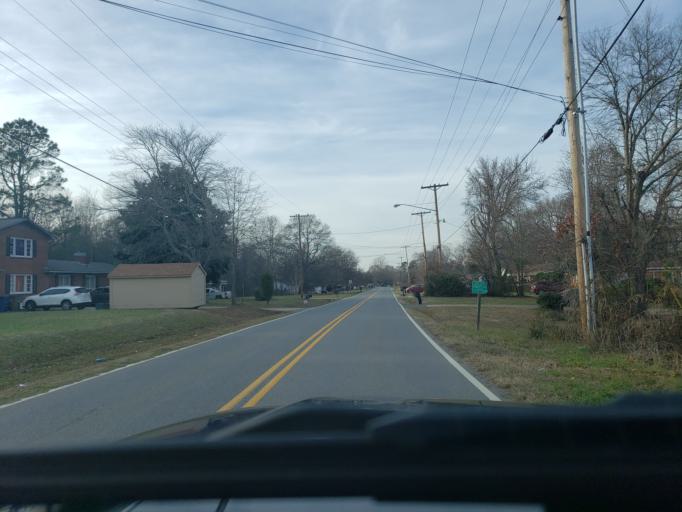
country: US
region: North Carolina
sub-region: Cleveland County
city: Shelby
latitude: 35.2748
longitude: -81.5032
